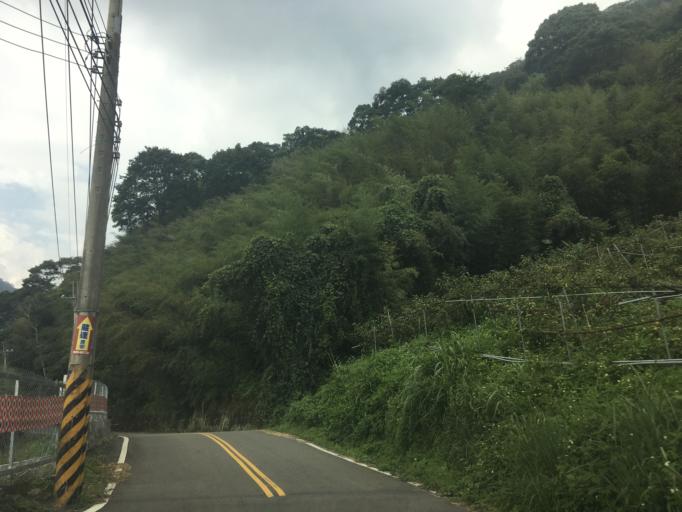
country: TW
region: Taiwan
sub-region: Miaoli
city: Miaoli
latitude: 24.3525
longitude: 120.9456
